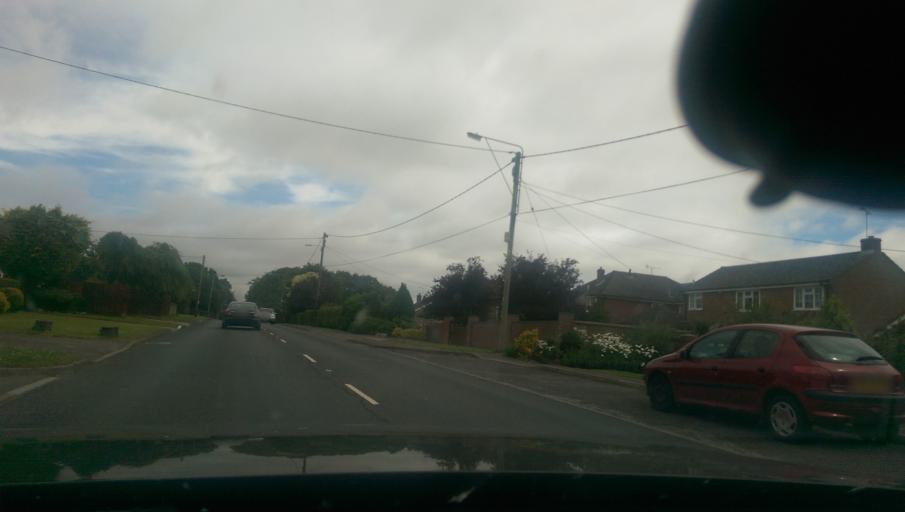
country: GB
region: England
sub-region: Wiltshire
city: Amesbury
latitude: 51.1843
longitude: -1.7831
